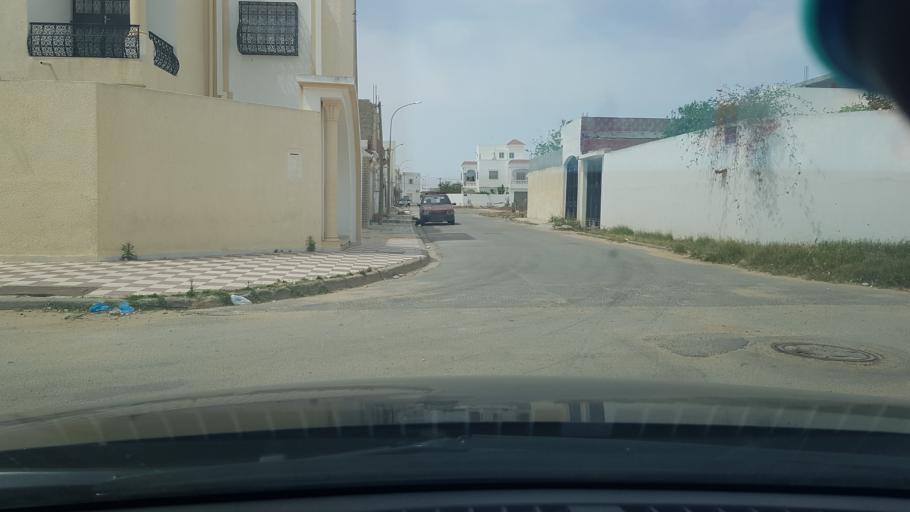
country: TN
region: Safaqis
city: Al Qarmadah
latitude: 34.8265
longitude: 10.7546
